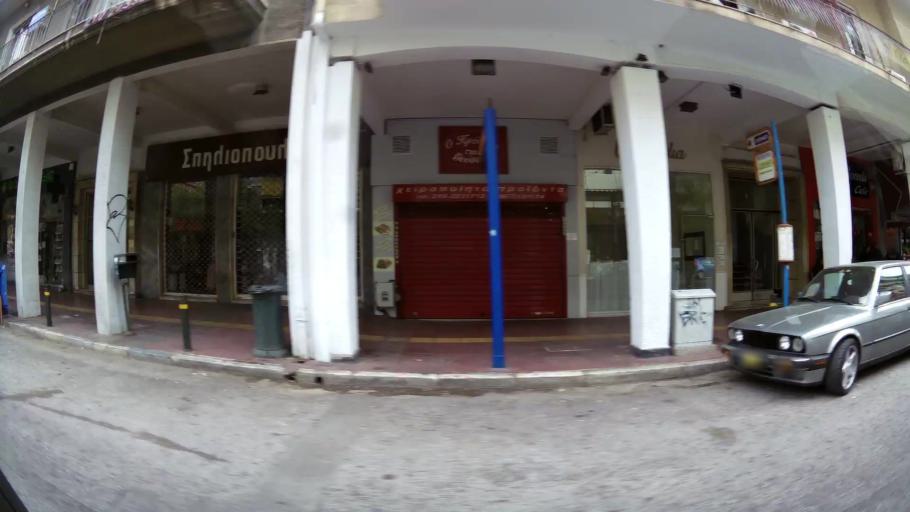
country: GR
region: Attica
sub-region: Nomarchia Athinas
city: Nea Chalkidona
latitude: 38.0183
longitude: 23.7355
